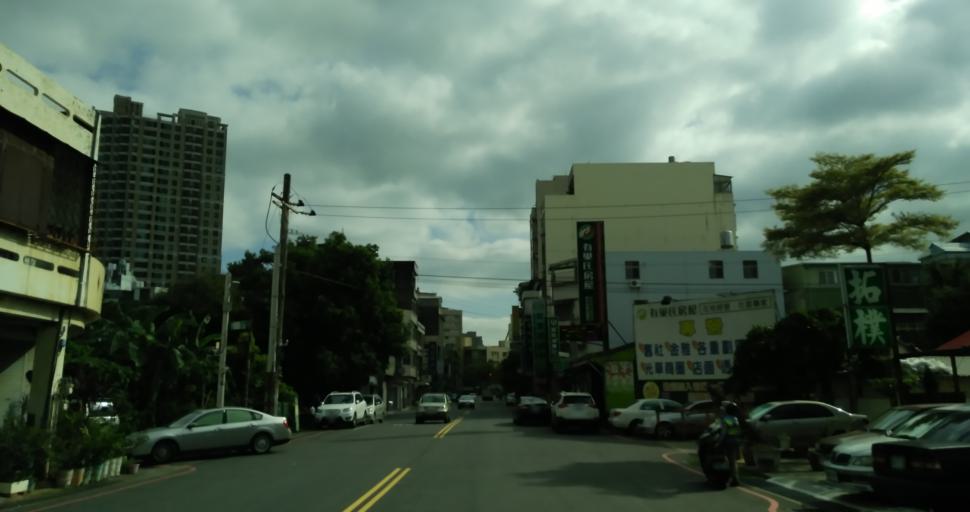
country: TW
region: Taiwan
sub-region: Hsinchu
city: Hsinchu
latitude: 24.8160
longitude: 120.9723
